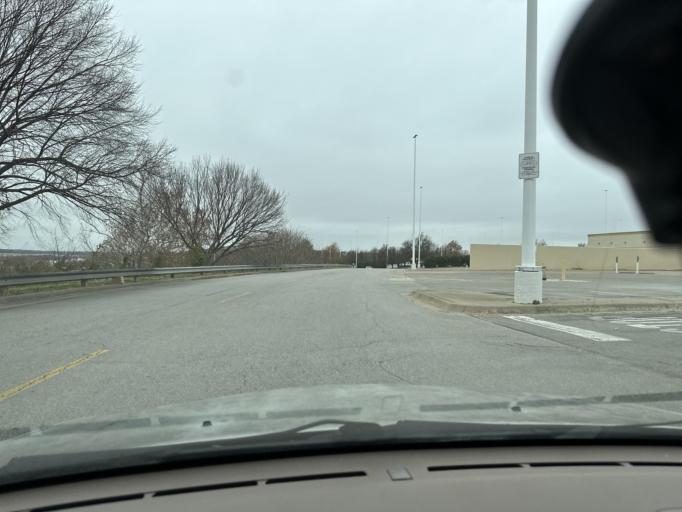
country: US
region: Arkansas
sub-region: Washington County
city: Johnson
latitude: 36.1259
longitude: -94.1474
